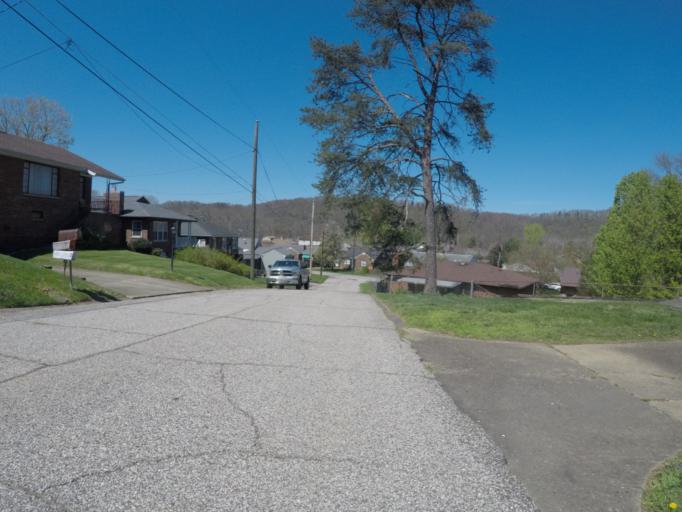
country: US
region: West Virginia
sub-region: Cabell County
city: Pea Ridge
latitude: 38.4217
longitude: -82.3064
